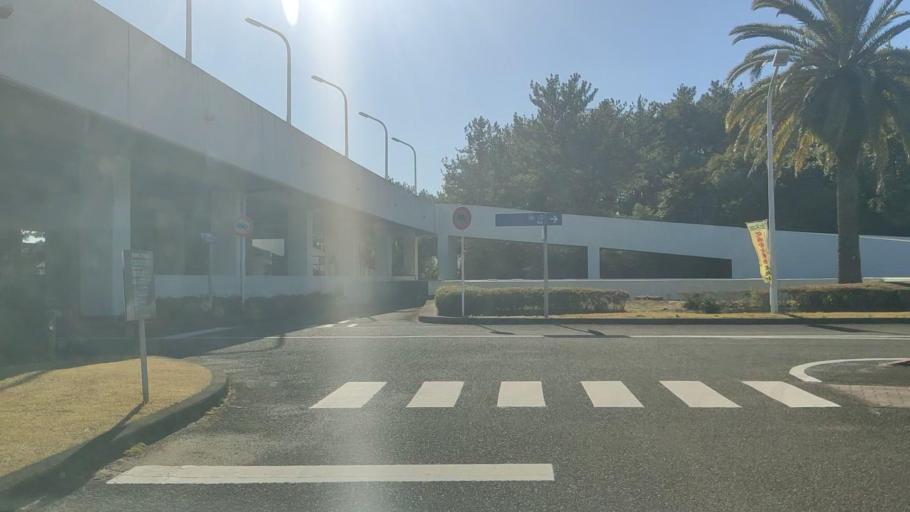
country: JP
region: Miyazaki
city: Miyazaki-shi
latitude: 31.9571
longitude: 131.4682
